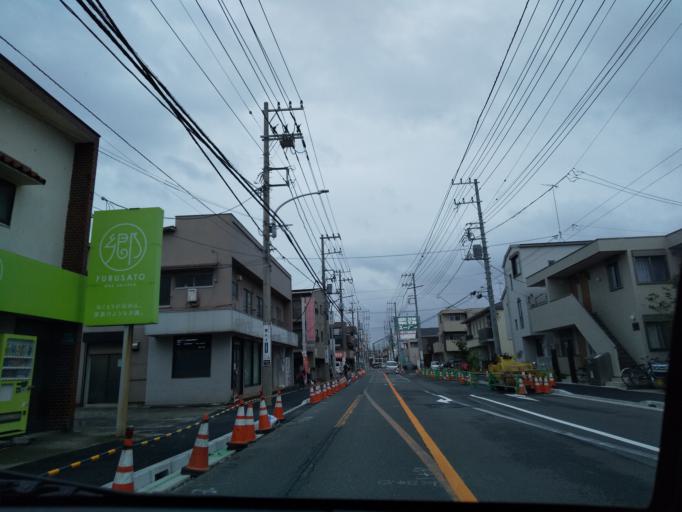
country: JP
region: Kanagawa
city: Fujisawa
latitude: 35.4068
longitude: 139.5009
